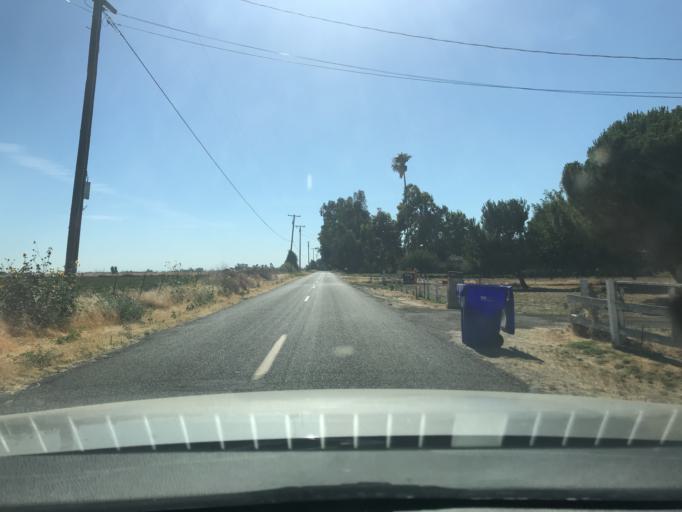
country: US
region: California
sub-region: Merced County
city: Atwater
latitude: 37.3389
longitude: -120.5436
